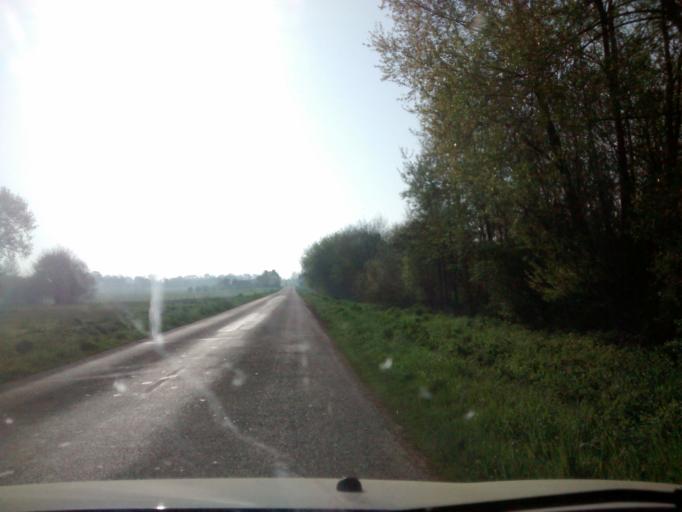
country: FR
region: Brittany
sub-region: Departement d'Ille-et-Vilaine
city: Saint-Jean-sur-Couesnon
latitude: 48.2790
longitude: -1.3694
